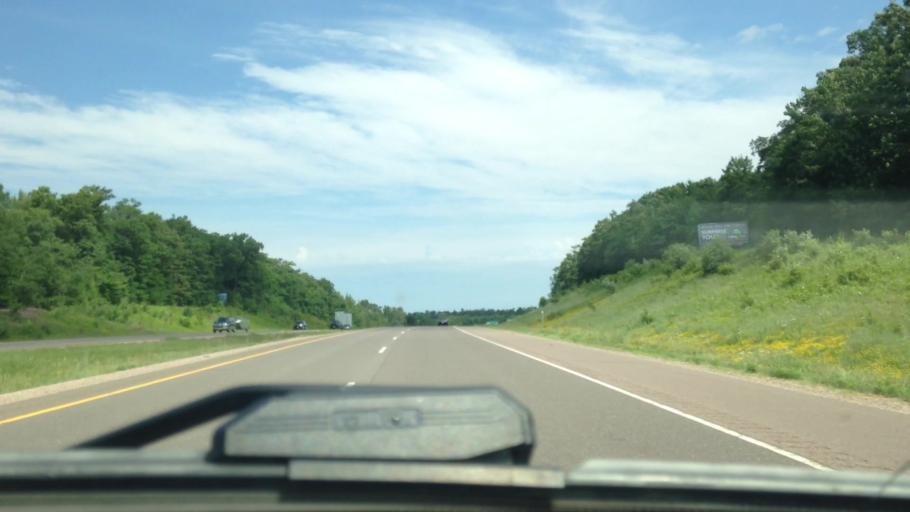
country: US
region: Wisconsin
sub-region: Washburn County
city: Spooner
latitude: 45.8341
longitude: -91.8594
